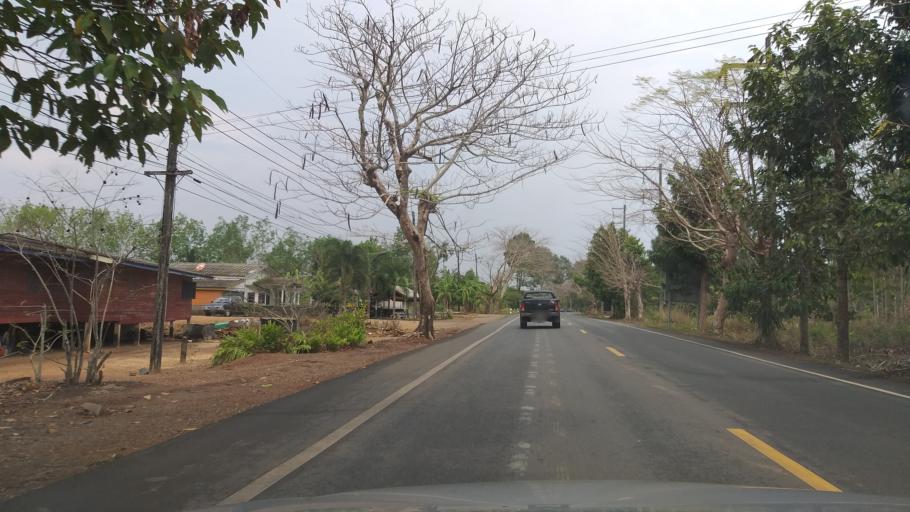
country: TH
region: Trat
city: Khao Saming
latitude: 12.3164
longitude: 102.3564
